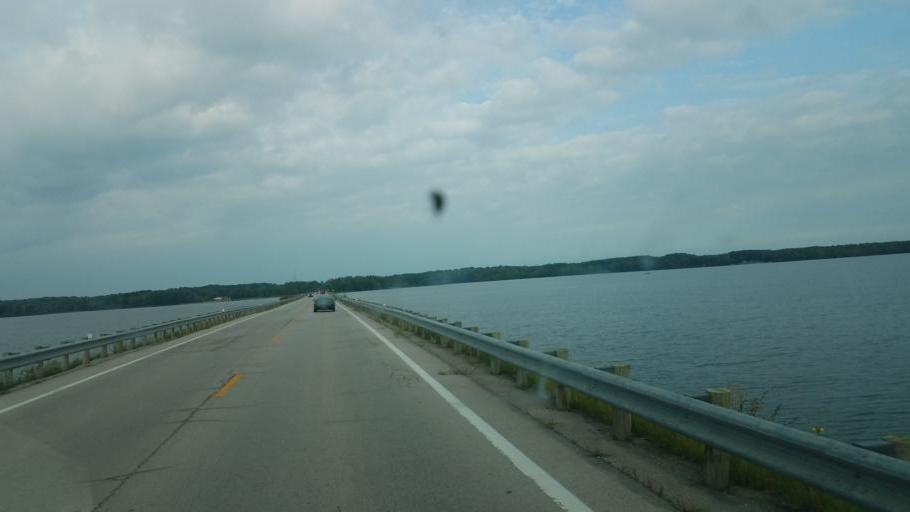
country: US
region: Pennsylvania
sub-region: Crawford County
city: Pymatuning Central
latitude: 41.6069
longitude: -80.5202
